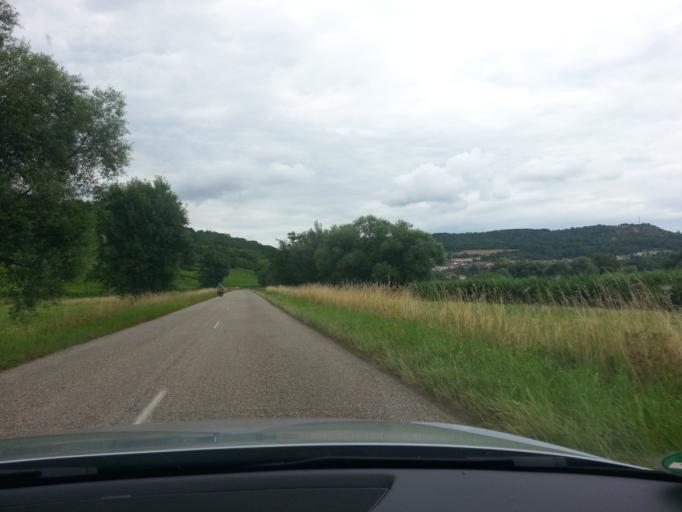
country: FR
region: Lorraine
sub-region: Departement de la Moselle
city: Sierck-les-Bains
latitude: 49.4511
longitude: 6.3285
